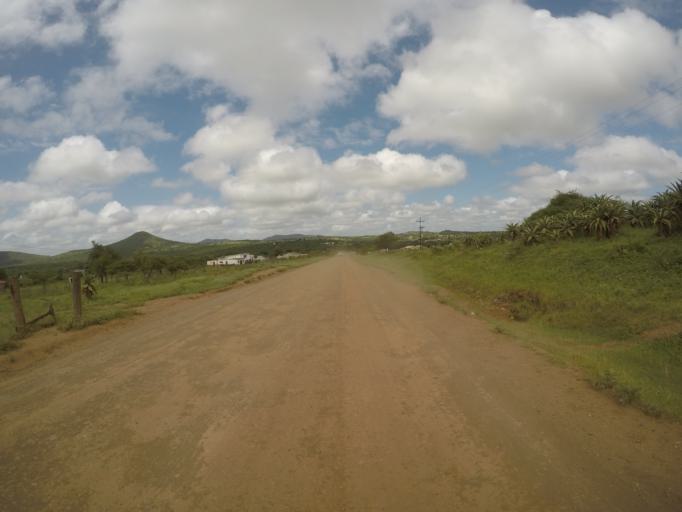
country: ZA
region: KwaZulu-Natal
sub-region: uThungulu District Municipality
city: Empangeni
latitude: -28.5834
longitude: 31.8457
